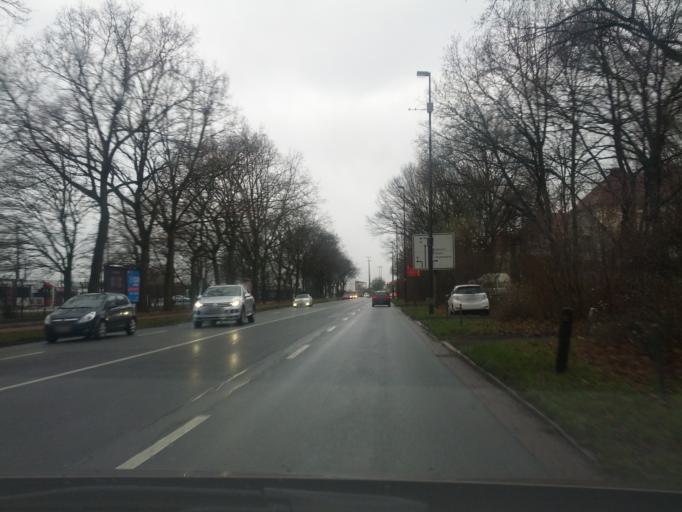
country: DE
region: Bremen
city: Bremen
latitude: 53.0607
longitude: 8.7911
